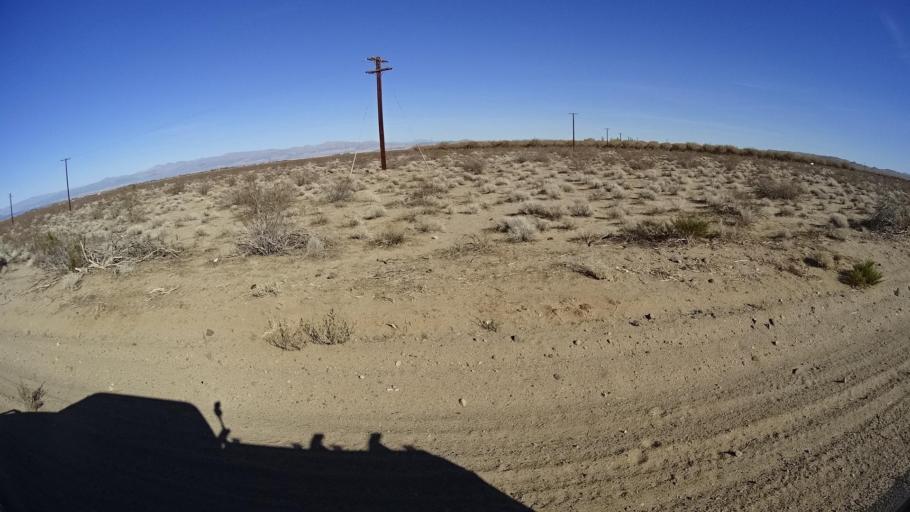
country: US
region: California
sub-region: Kern County
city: China Lake Acres
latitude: 35.5921
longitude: -117.7945
